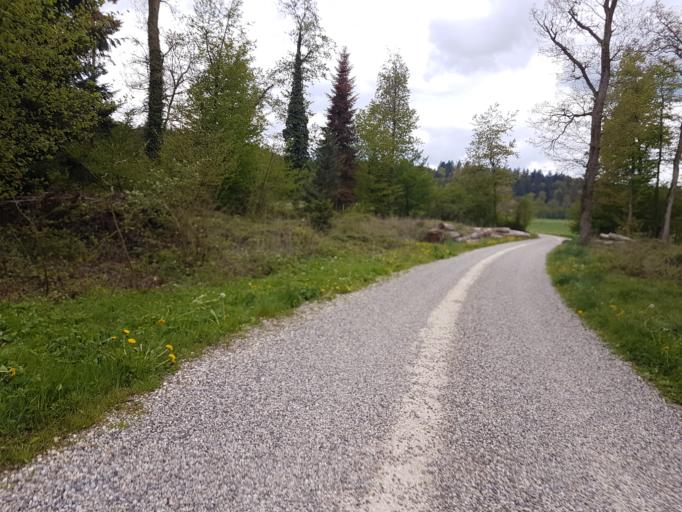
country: CH
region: Bern
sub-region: Oberaargau
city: Aarwangen
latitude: 47.2376
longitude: 7.7535
